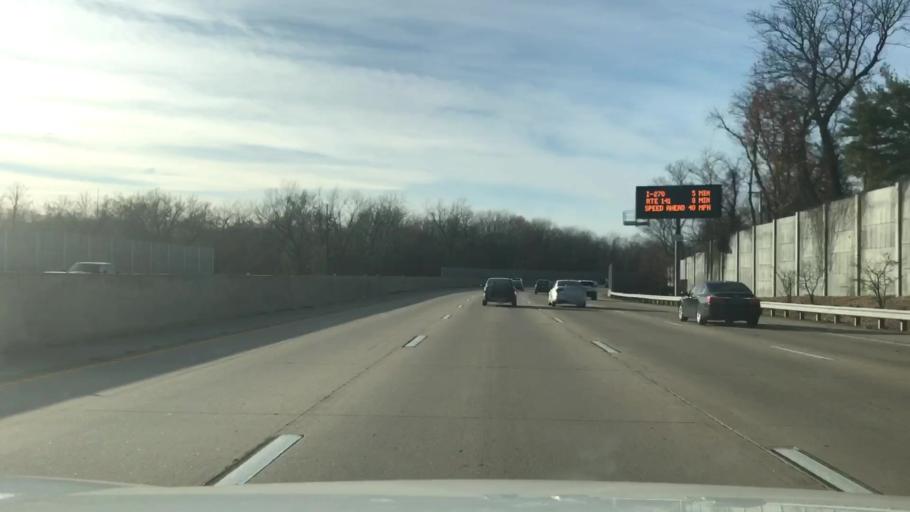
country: US
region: Missouri
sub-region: Saint Louis County
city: Ladue
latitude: 38.6315
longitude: -90.3838
